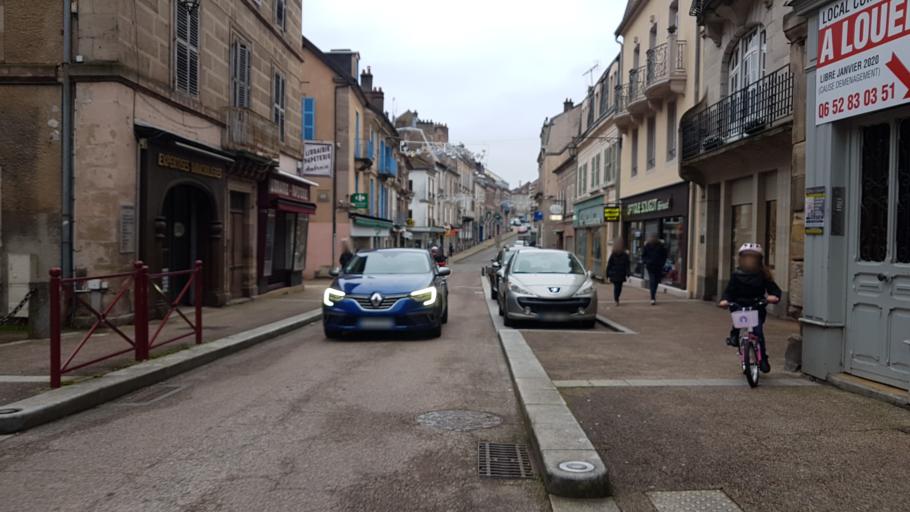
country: FR
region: Franche-Comte
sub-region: Departement de la Haute-Saone
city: Saint-Sauveur
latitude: 47.8162
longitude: 6.3807
